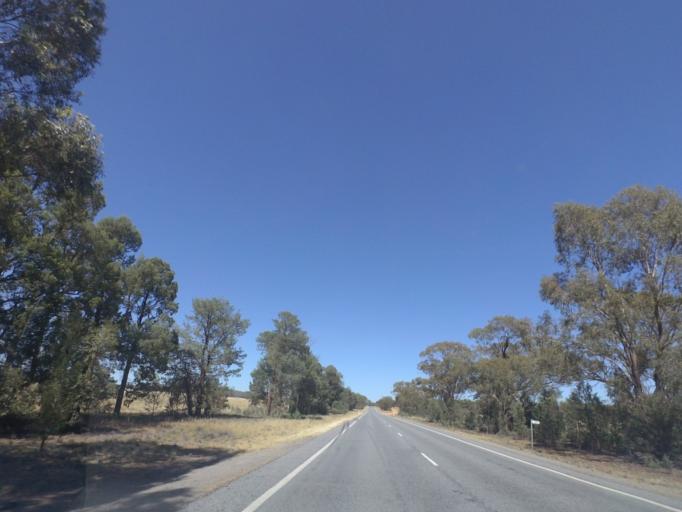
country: AU
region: New South Wales
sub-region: Narrandera
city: Narrandera
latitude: -34.4166
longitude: 146.8567
